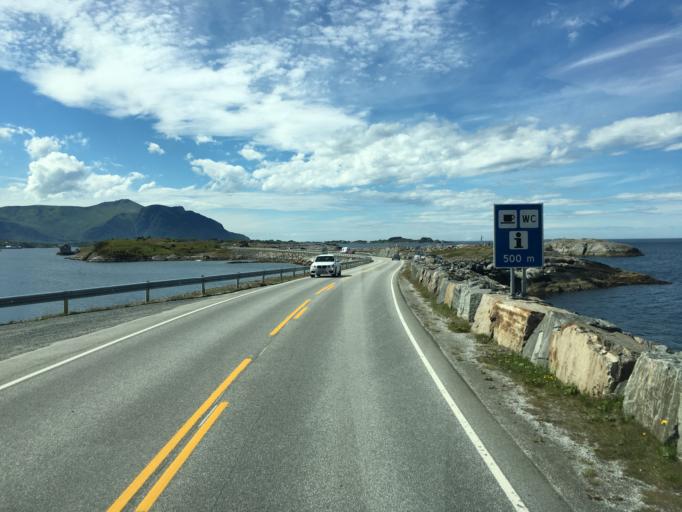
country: NO
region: More og Romsdal
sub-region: Eide
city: Eide
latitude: 63.0153
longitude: 7.3402
